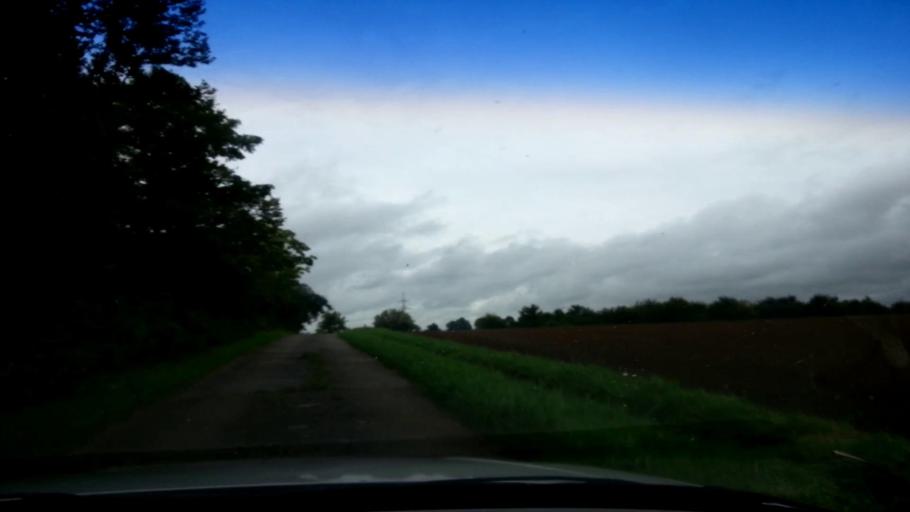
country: DE
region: Bavaria
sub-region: Upper Franconia
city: Memmelsdorf
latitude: 49.9525
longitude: 10.9797
